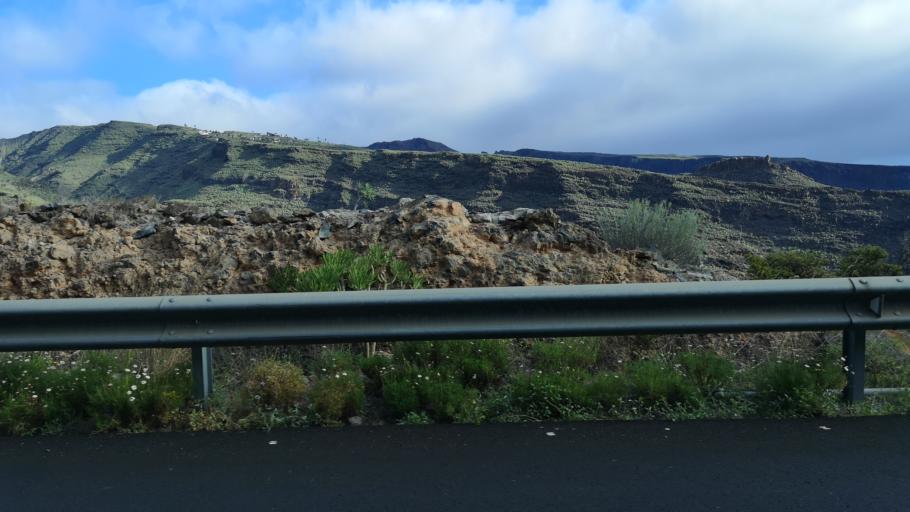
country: ES
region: Canary Islands
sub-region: Provincia de Santa Cruz de Tenerife
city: Alajero
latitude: 28.0544
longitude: -17.2003
